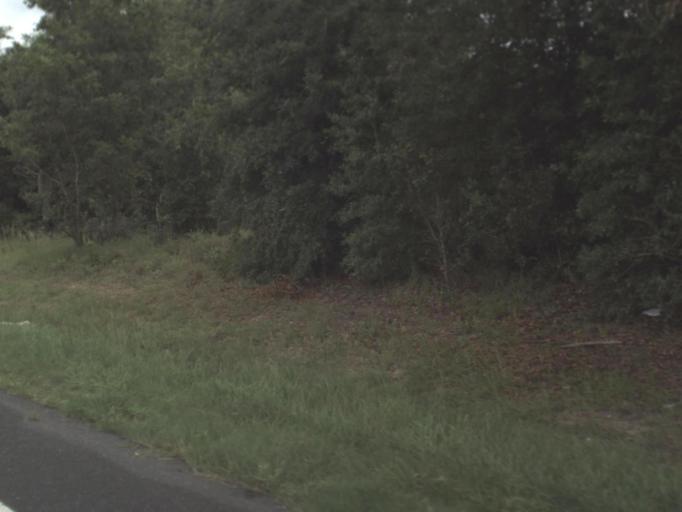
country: US
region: Florida
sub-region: Levy County
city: Williston
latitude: 29.3020
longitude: -82.4489
